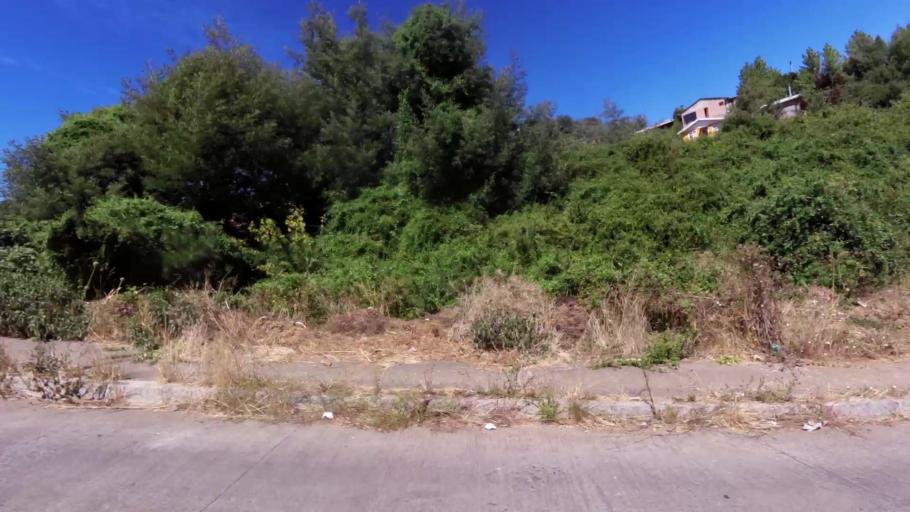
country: CL
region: Biobio
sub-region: Provincia de Concepcion
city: Penco
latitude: -36.7382
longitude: -72.9865
